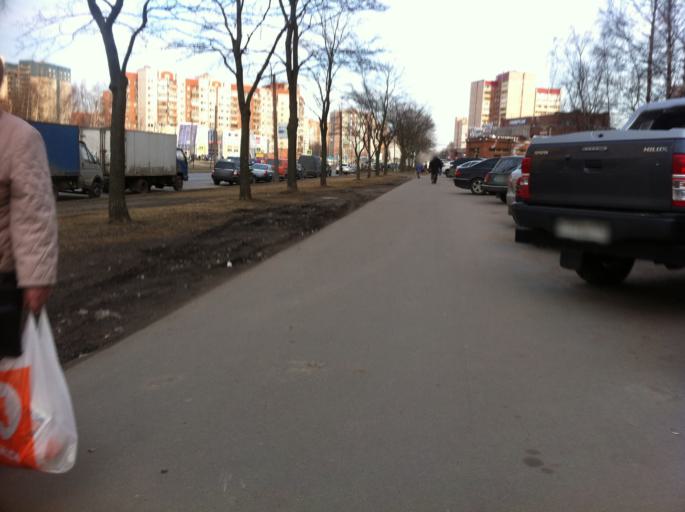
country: RU
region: St.-Petersburg
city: Uritsk
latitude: 59.8542
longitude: 30.1901
